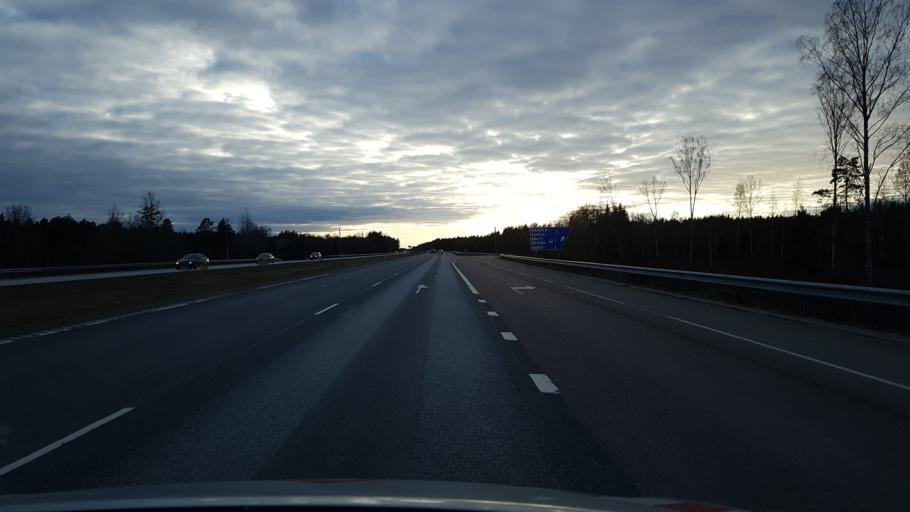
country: EE
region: Harju
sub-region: Kuusalu vald
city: Kuusalu
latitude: 59.4568
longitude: 25.5261
